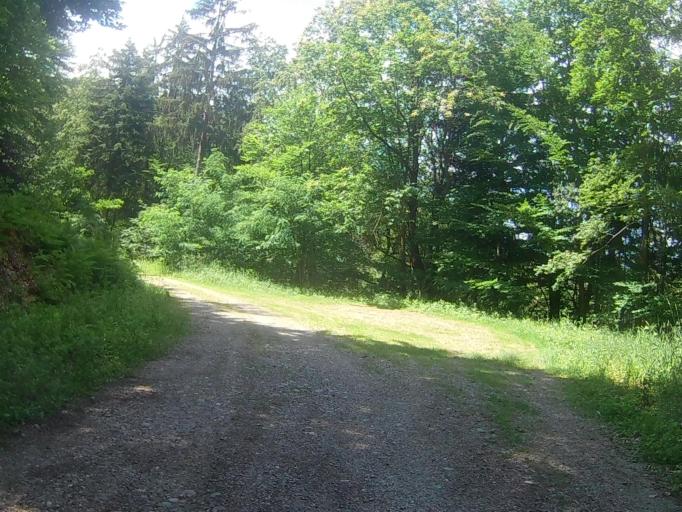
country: SI
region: Selnica ob Dravi
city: Selnica ob Dravi
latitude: 46.5232
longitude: 15.4902
